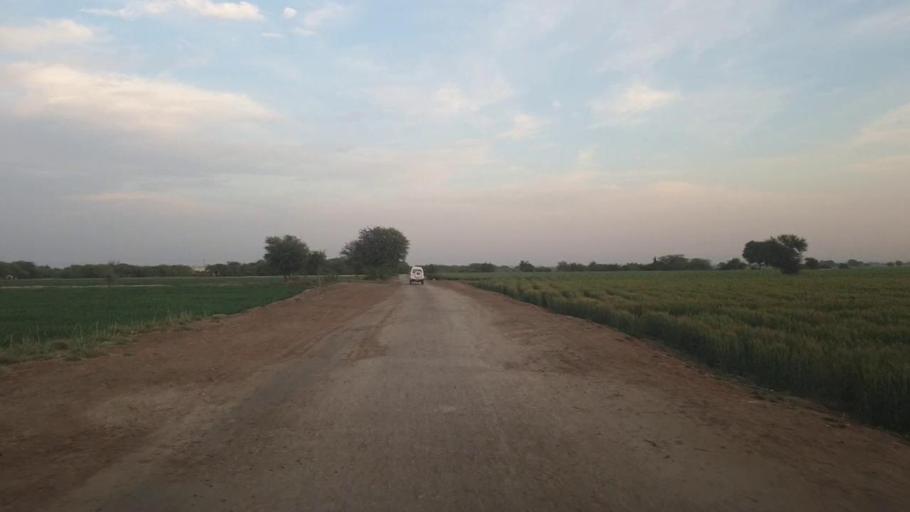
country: PK
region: Sindh
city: Umarkot
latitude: 25.2647
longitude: 69.6737
